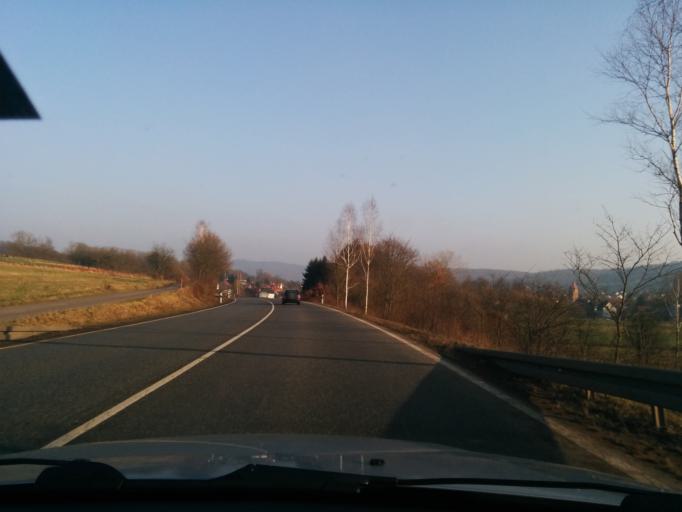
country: DE
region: Hesse
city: Waldkappel
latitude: 51.1430
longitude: 9.9258
